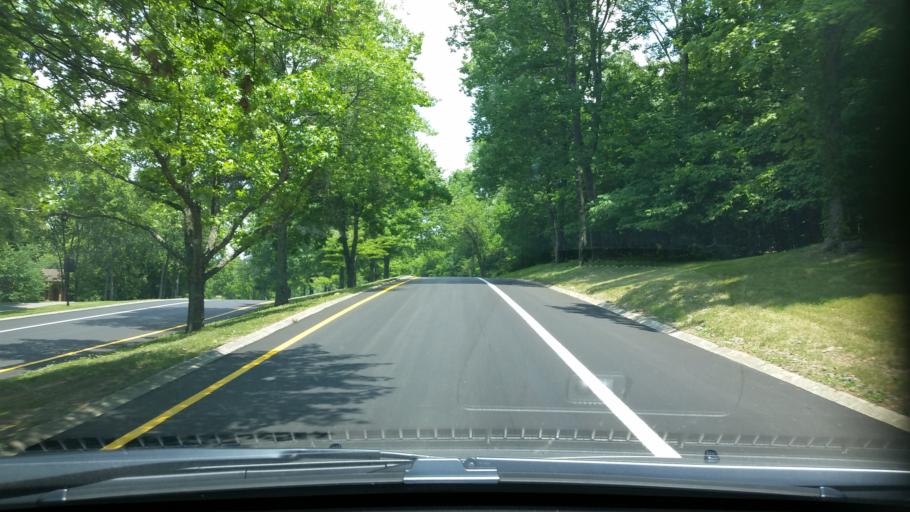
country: US
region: Tennessee
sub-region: Williamson County
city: Brentwood Estates
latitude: 35.9764
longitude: -86.7544
